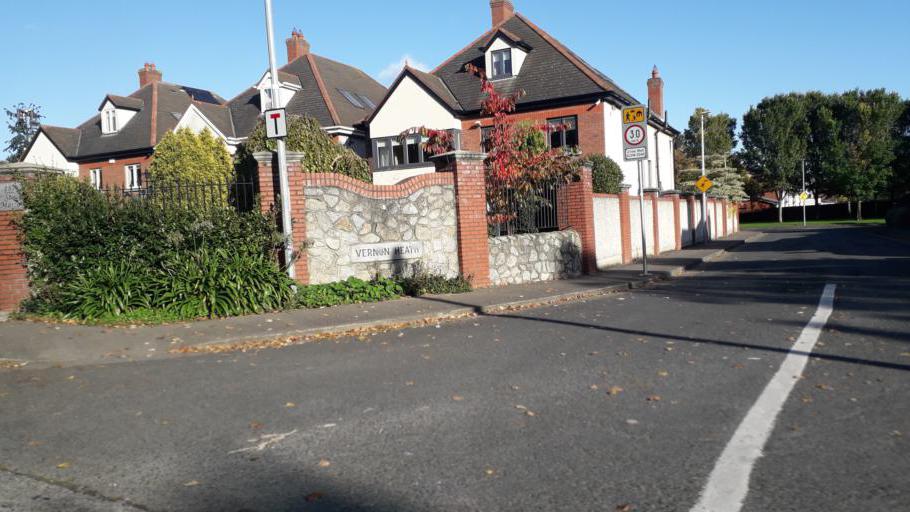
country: IE
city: Killester
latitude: 53.3685
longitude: -6.1946
